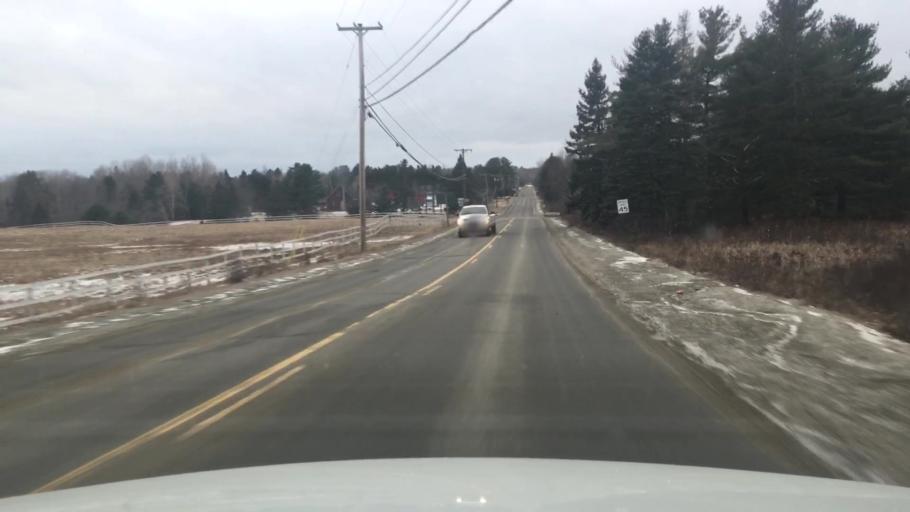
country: US
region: Maine
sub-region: Hancock County
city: Trenton
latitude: 44.5008
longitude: -68.3477
